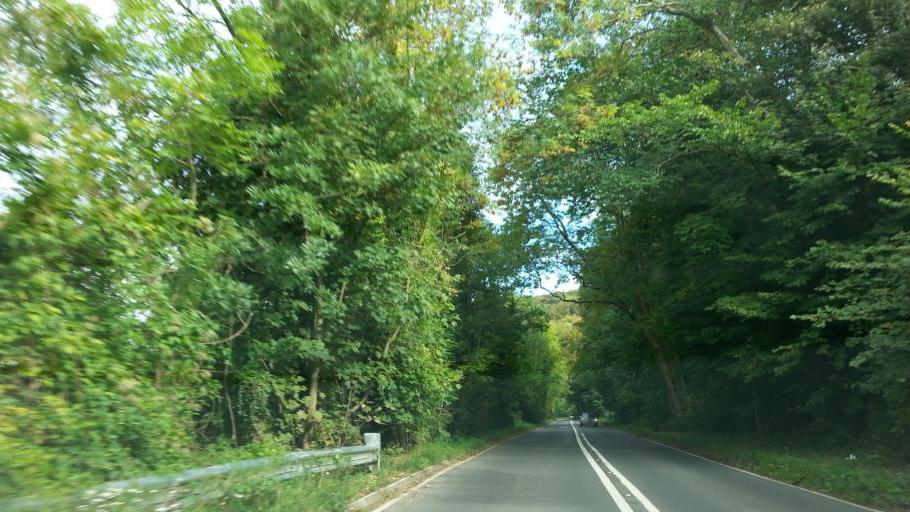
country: GB
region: England
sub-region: Gloucestershire
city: Painswick
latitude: 51.8244
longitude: -2.1696
